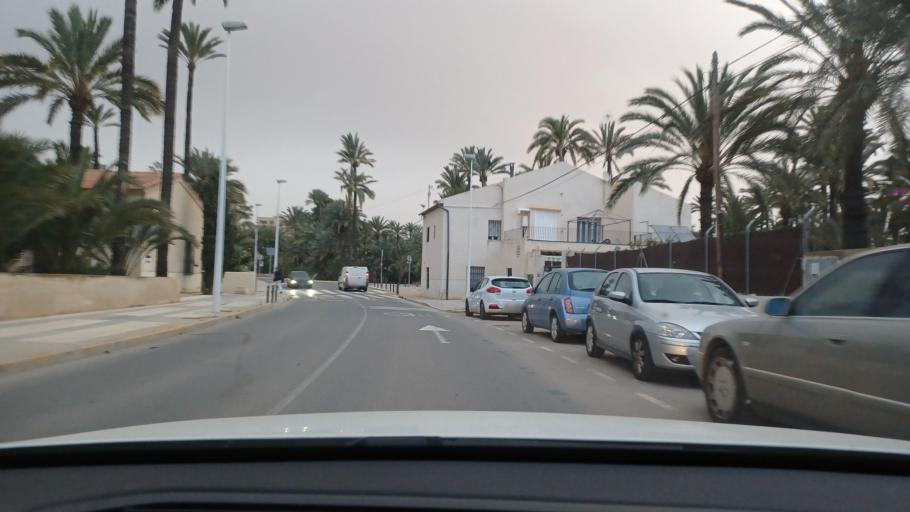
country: ES
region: Valencia
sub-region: Provincia de Alicante
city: Elche
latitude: 38.2598
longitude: -0.6930
